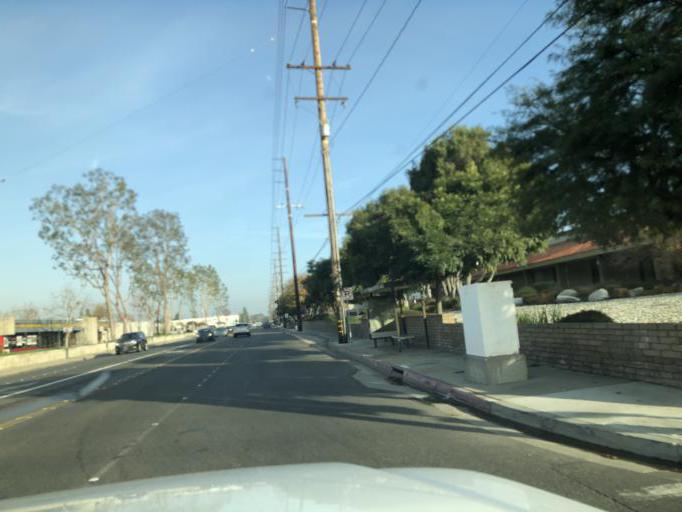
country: US
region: California
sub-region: Orange County
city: Fountain Valley
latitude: 33.6942
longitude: -117.9454
